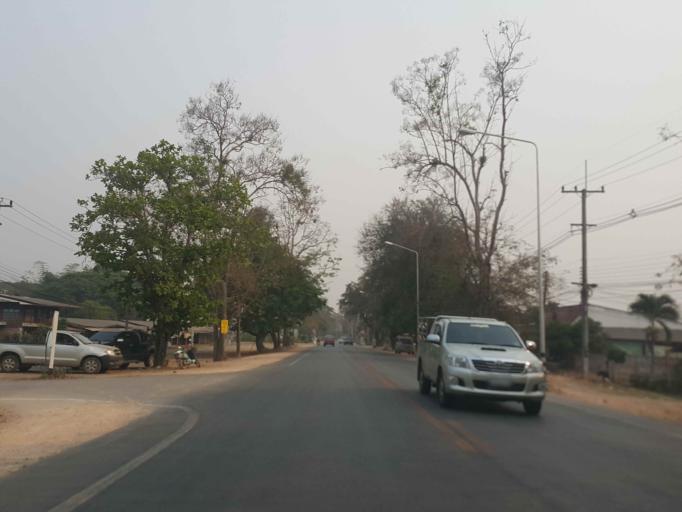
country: TH
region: Chiang Mai
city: Mae Taeng
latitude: 18.9961
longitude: 98.9772
